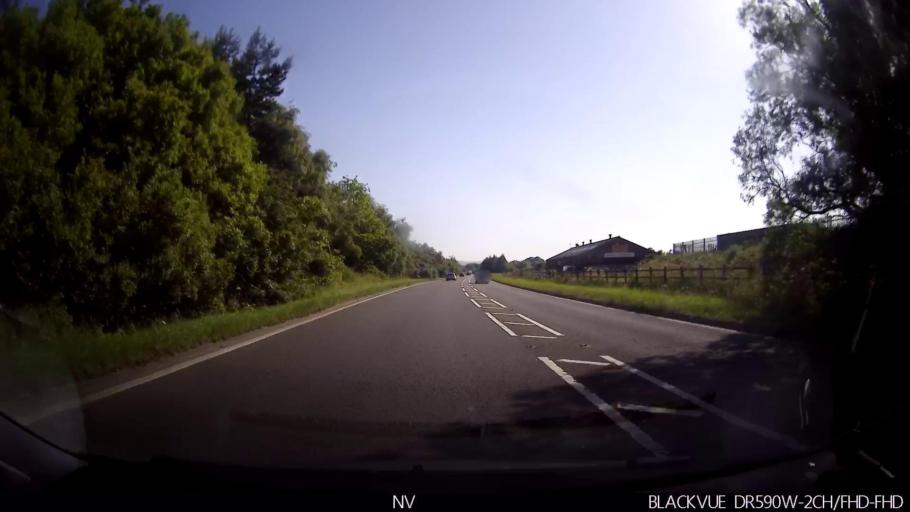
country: GB
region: England
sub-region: North Yorkshire
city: Scarborough
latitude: 54.2403
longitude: -0.4166
